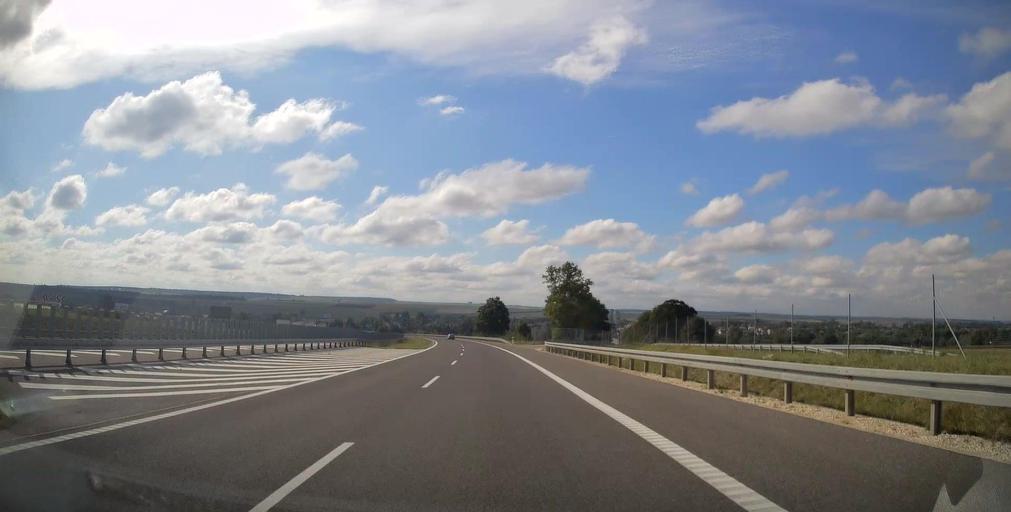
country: PL
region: Swietokrzyskie
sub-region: Powiat jedrzejowski
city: Wodzislaw
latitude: 50.5295
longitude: 20.1945
